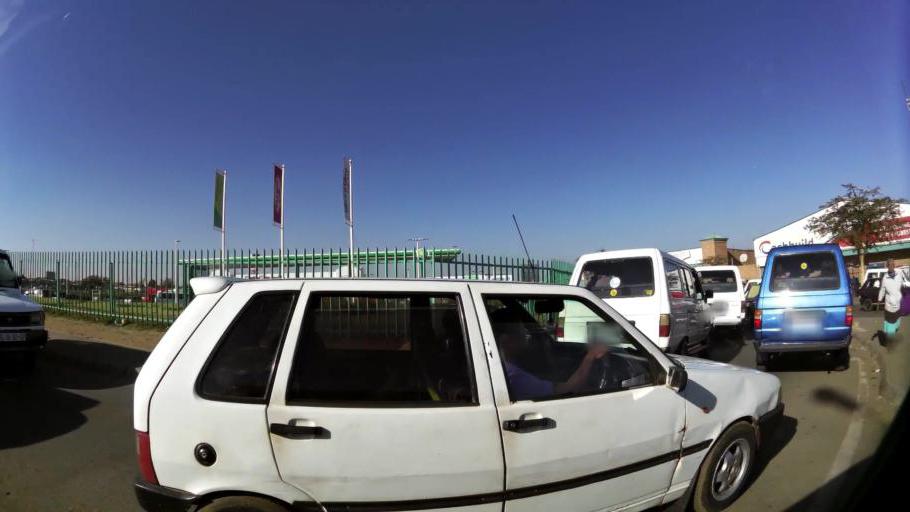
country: ZA
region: Gauteng
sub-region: City of Tshwane Metropolitan Municipality
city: Mabopane
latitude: -25.5808
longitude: 28.1028
